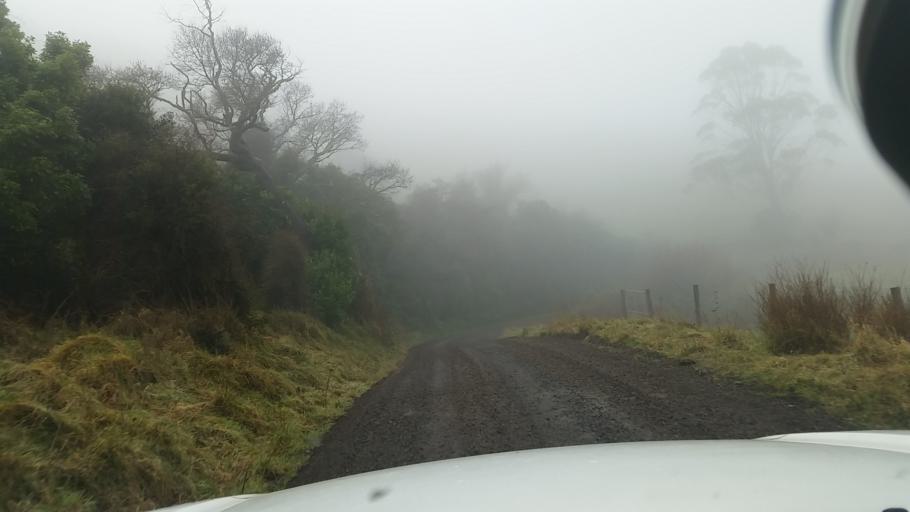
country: NZ
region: Canterbury
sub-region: Christchurch City
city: Christchurch
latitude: -43.7410
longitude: 172.9020
